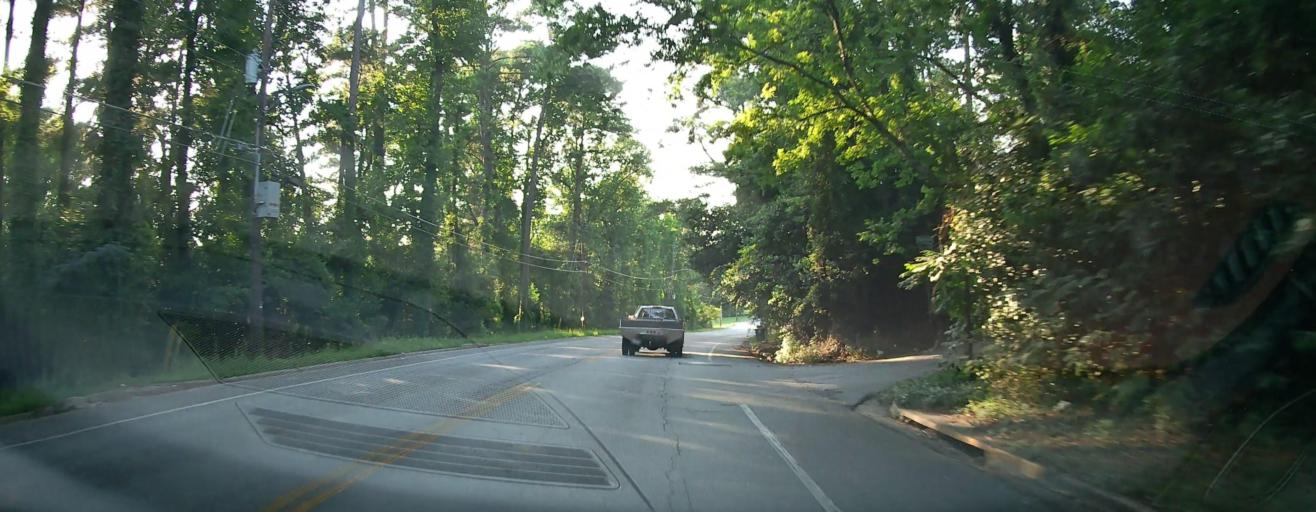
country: US
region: Georgia
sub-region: Bibb County
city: Macon
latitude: 32.8606
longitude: -83.6946
